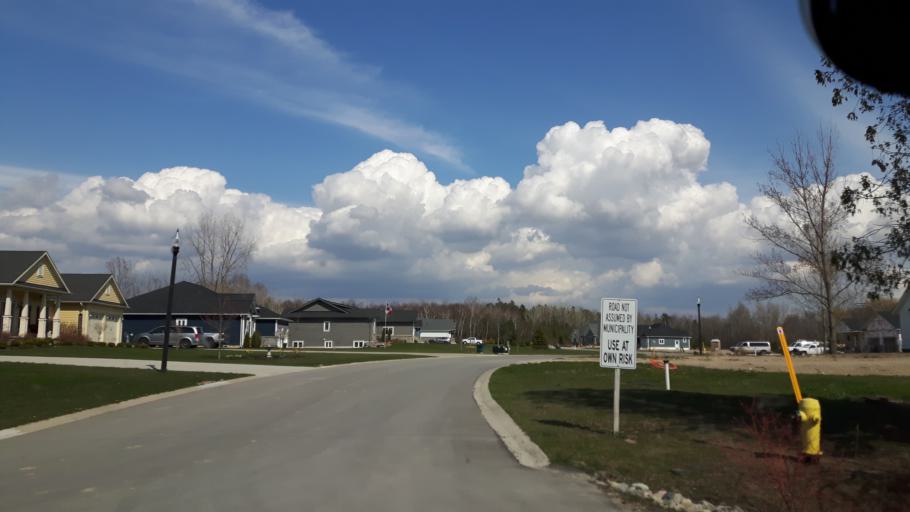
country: CA
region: Ontario
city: Bluewater
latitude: 43.5516
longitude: -81.7007
